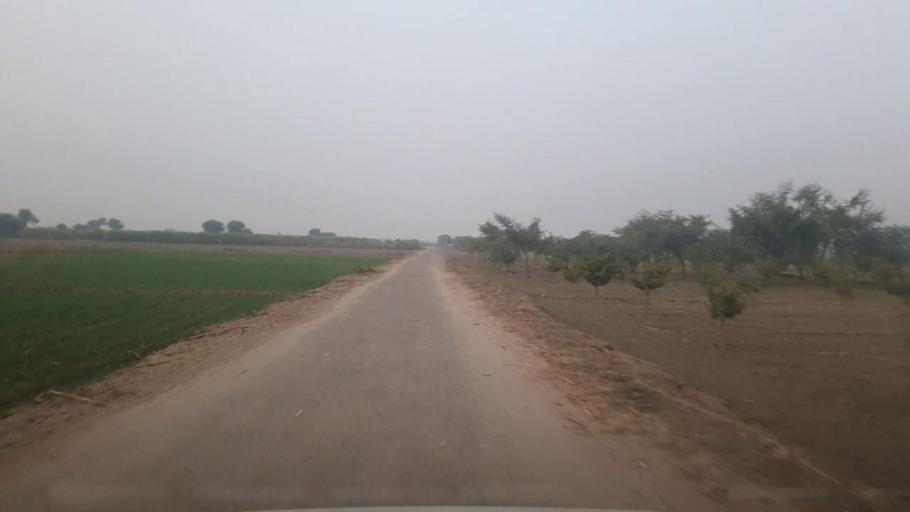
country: PK
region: Sindh
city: Kot Diji
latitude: 27.3374
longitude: 68.6171
